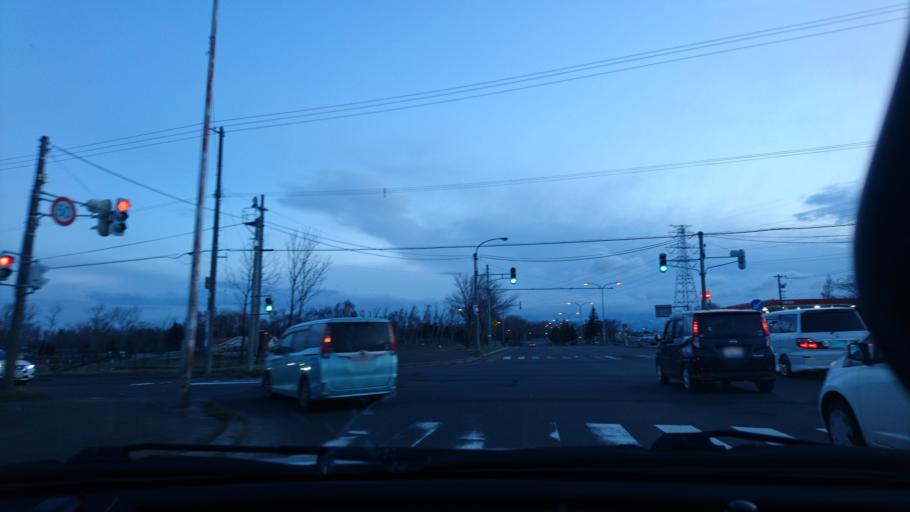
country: JP
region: Hokkaido
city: Sapporo
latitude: 43.1231
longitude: 141.4142
